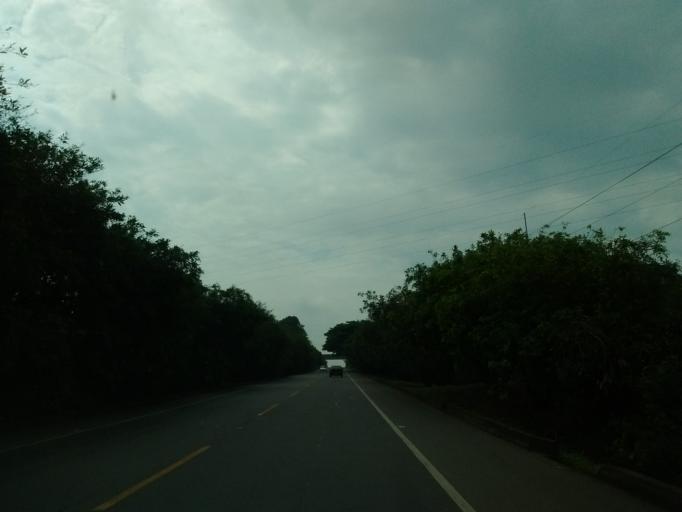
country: CO
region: Cauca
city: Santander de Quilichao
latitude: 3.0129
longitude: -76.4991
